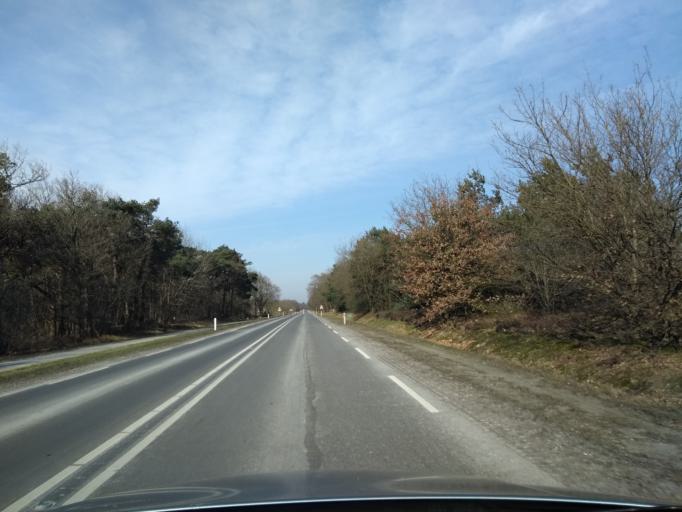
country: DE
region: Lower Saxony
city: Wielen
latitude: 52.4730
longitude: 6.7010
